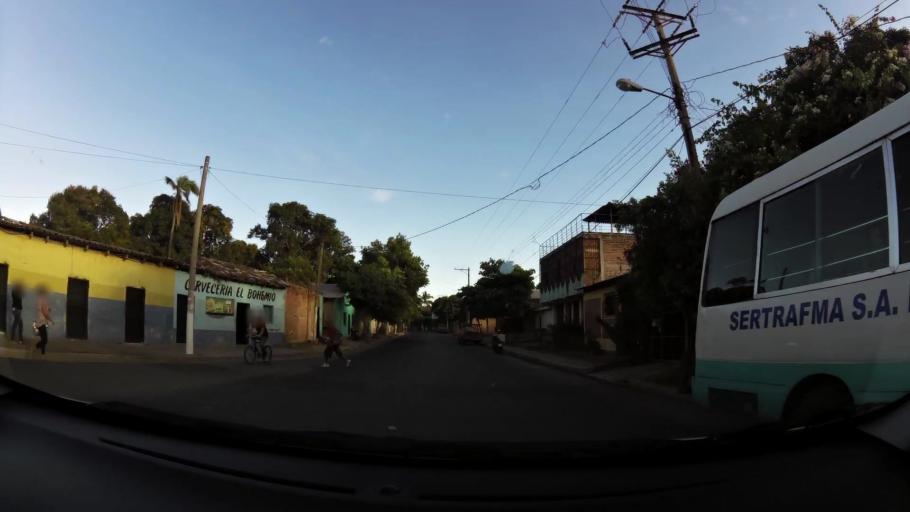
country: SV
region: Santa Ana
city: Metapan
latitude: 14.3298
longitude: -89.4494
